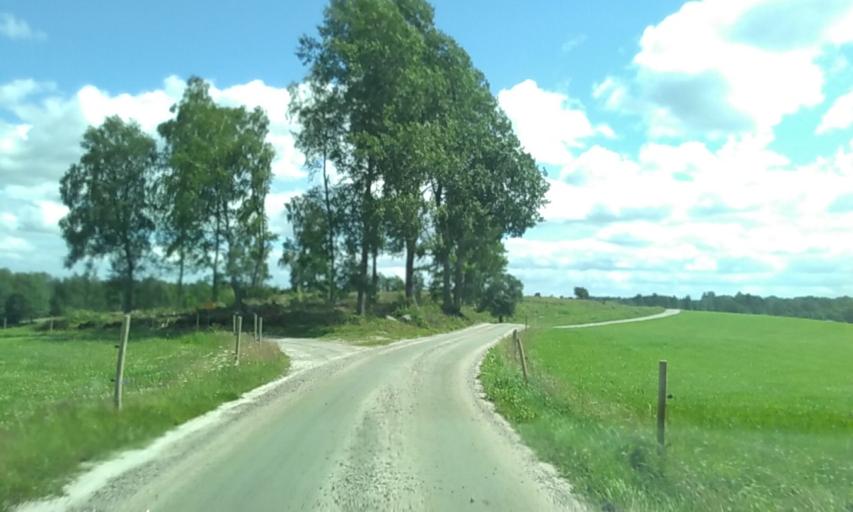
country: SE
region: Vaestra Goetaland
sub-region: Vargarda Kommun
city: Vargarda
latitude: 58.0409
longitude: 12.8451
